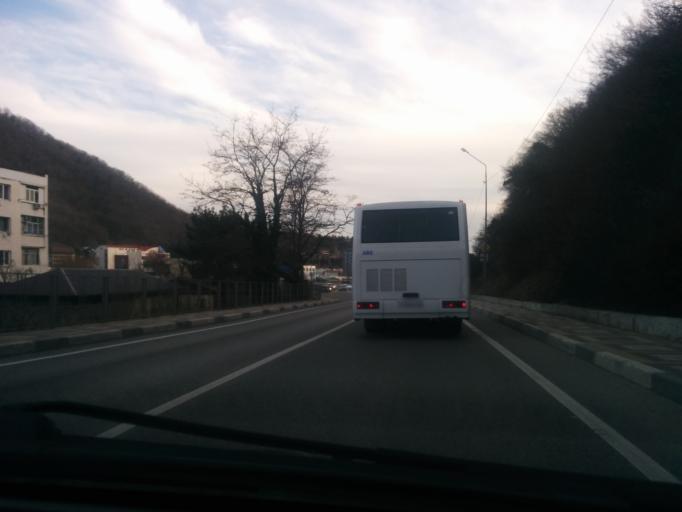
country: RU
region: Krasnodarskiy
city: Ol'ginka
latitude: 44.2008
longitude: 38.8873
